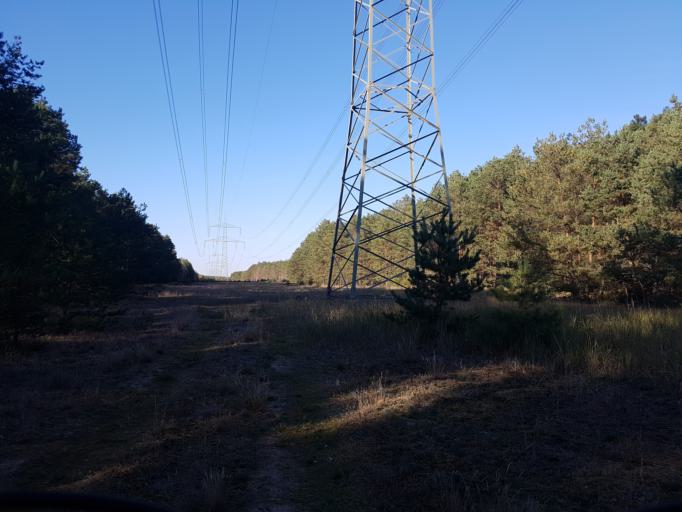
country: DE
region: Brandenburg
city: Schilda
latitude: 51.6196
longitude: 13.3686
